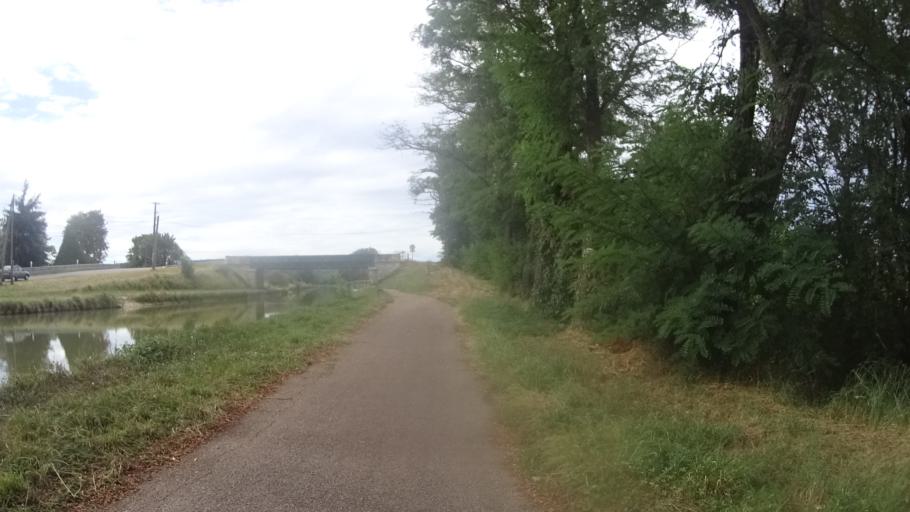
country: FR
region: Bourgogne
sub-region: Departement de la Nievre
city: Saint-Eloi
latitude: 46.9334
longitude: 3.2198
